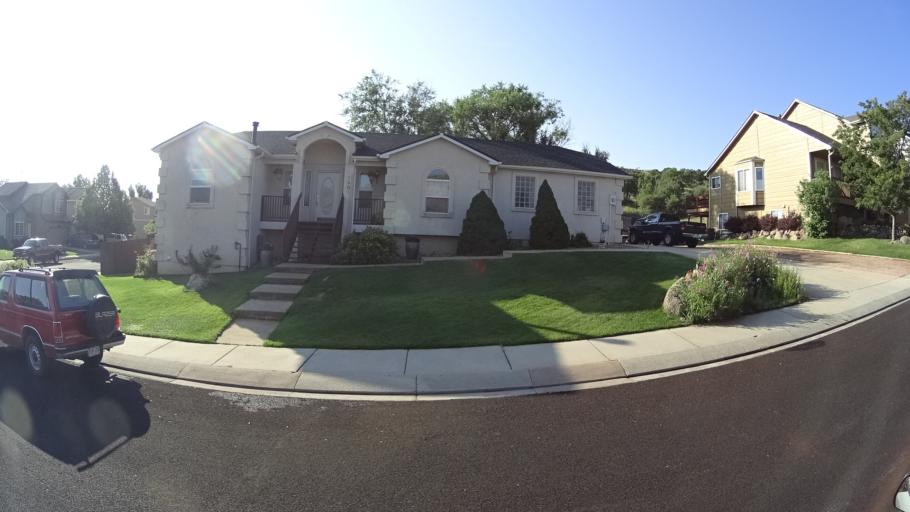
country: US
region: Colorado
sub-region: El Paso County
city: Colorado Springs
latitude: 38.8903
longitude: -104.8560
